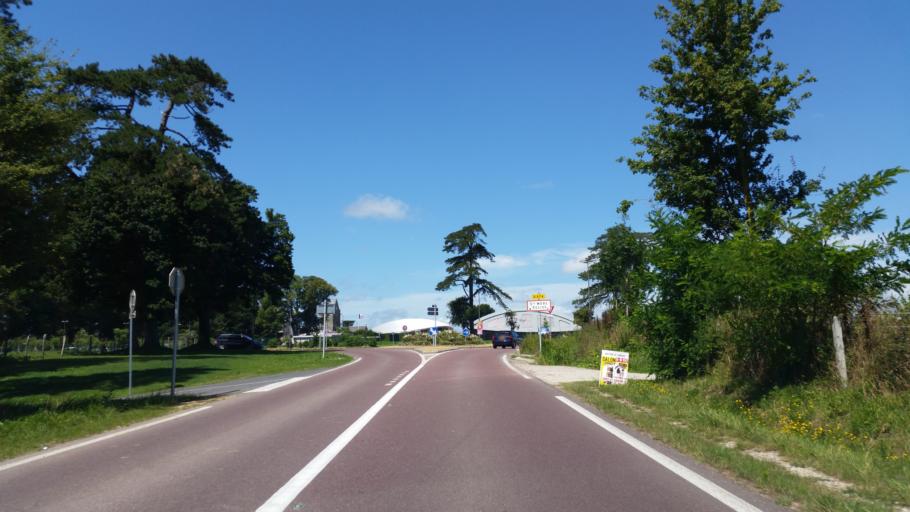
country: FR
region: Lower Normandy
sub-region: Departement de la Manche
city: Sainte-Mere-Eglise
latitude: 49.4067
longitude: -1.3120
